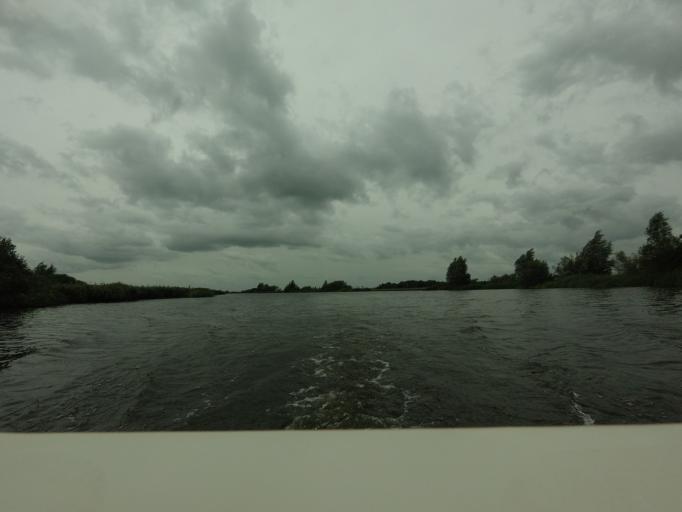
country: NL
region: Friesland
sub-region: Gemeente Boarnsterhim
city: Warten
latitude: 53.1010
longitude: 5.9121
